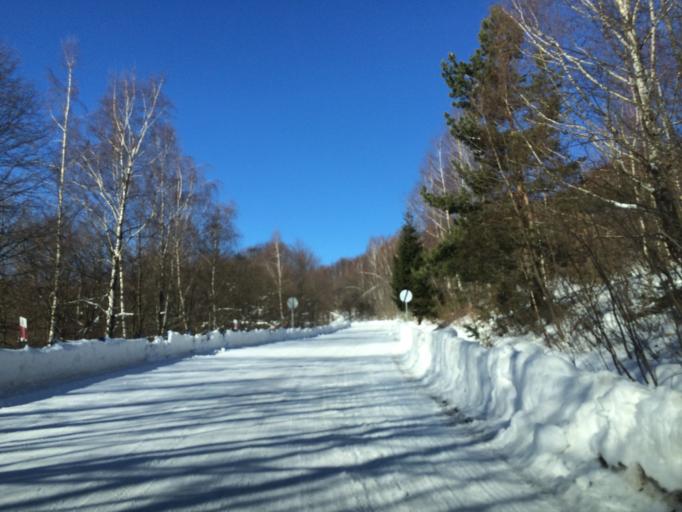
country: PL
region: Subcarpathian Voivodeship
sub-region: Powiat bieszczadzki
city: Lutowiska
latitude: 49.1209
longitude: 22.6065
